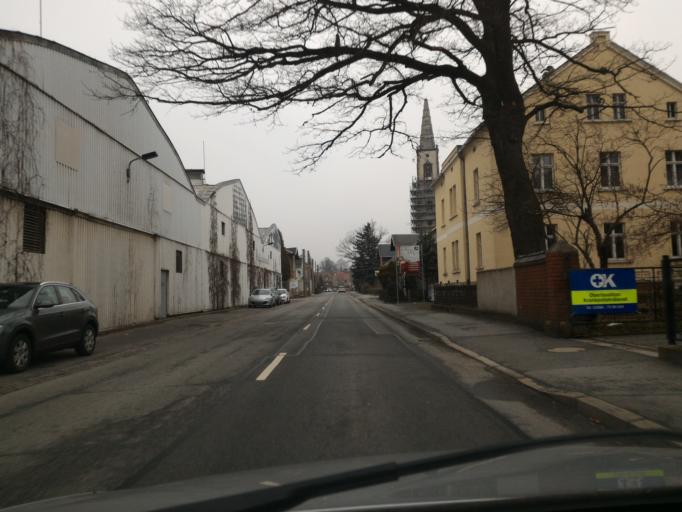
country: DE
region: Saxony
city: Leutersdorf
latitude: 50.9581
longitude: 14.6522
